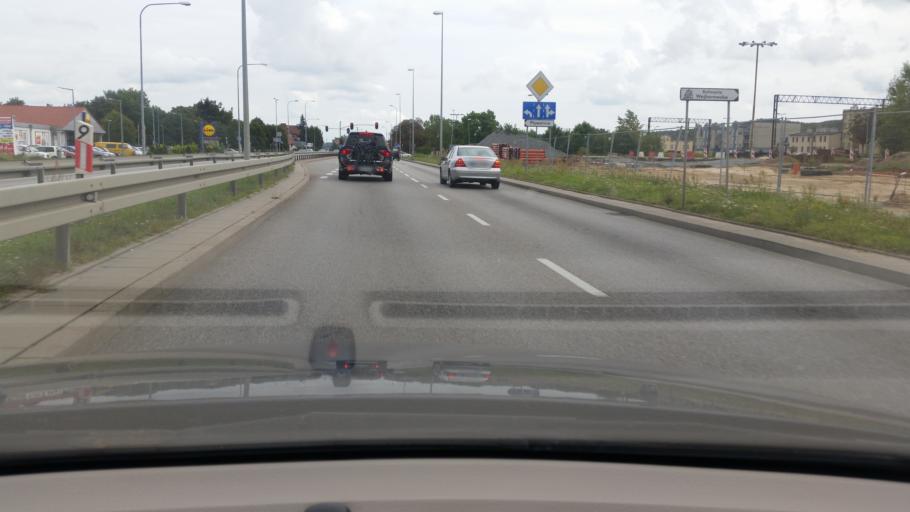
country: PL
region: Pomeranian Voivodeship
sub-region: Powiat wejherowski
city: Wejherowo
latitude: 54.6066
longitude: 18.2309
